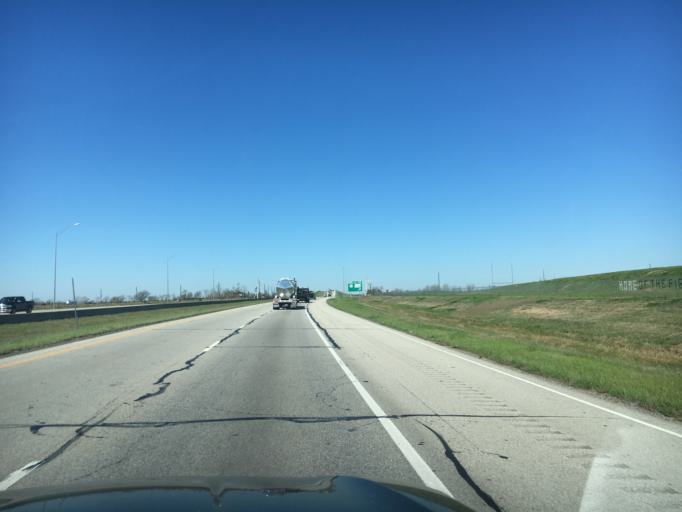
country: US
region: Texas
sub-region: Austin County
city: Sealy
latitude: 29.7604
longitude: -96.1755
